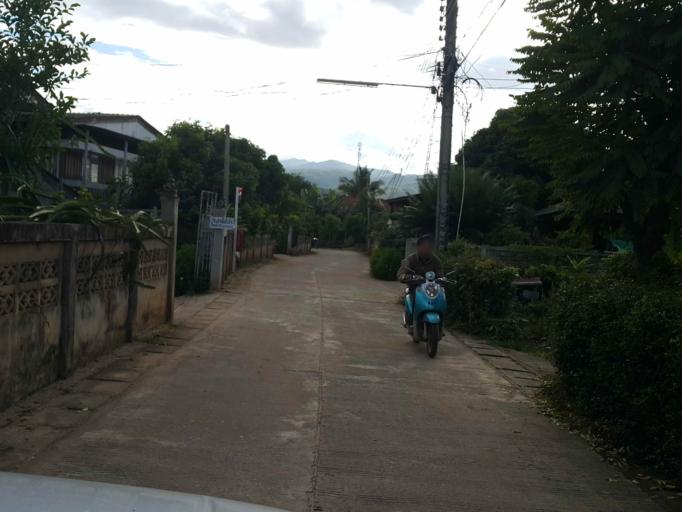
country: TH
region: Chiang Mai
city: Mae Chaem
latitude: 18.4982
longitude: 98.3679
